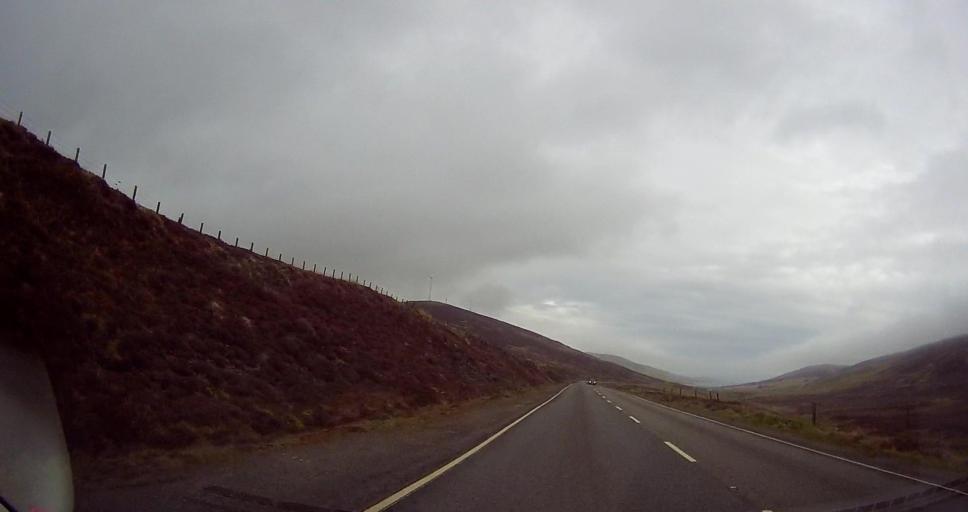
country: GB
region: Scotland
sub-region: Shetland Islands
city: Lerwick
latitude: 60.1511
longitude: -1.2368
